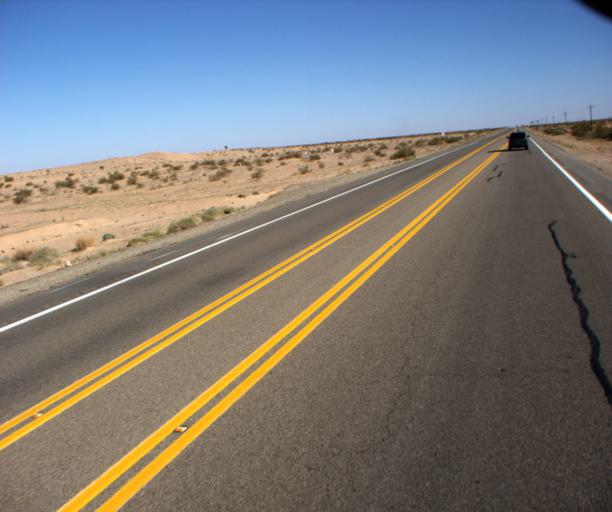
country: US
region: Arizona
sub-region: Yuma County
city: Fortuna Foothills
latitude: 32.8071
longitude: -114.3800
